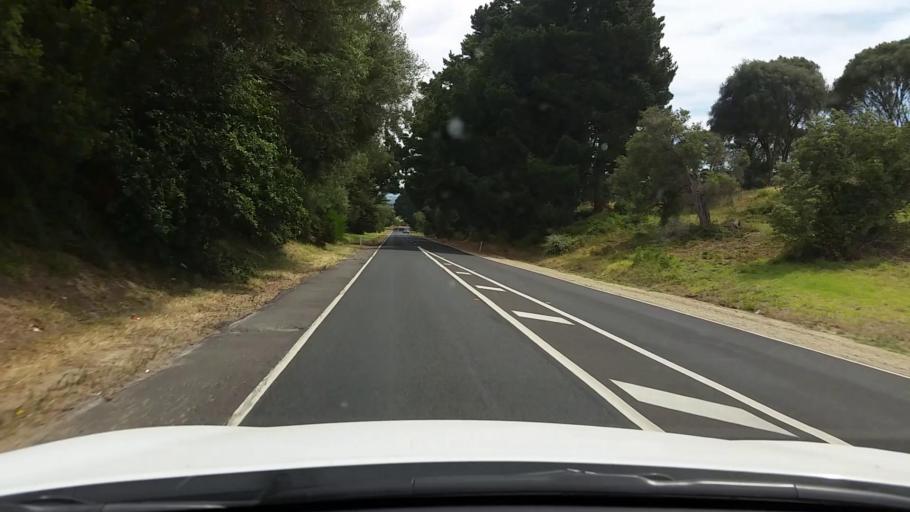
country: AU
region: Victoria
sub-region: Mornington Peninsula
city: Saint Andrews Beach
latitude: -38.4546
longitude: 144.8986
